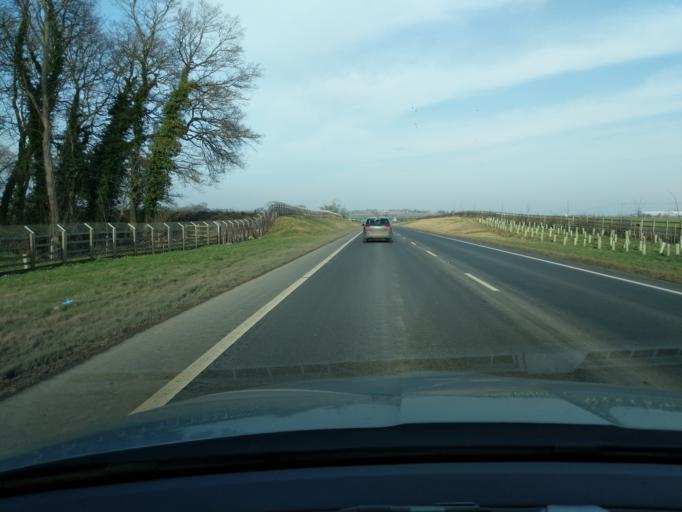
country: GB
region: England
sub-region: North Yorkshire
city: Bedale
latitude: 54.3001
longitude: -1.5874
